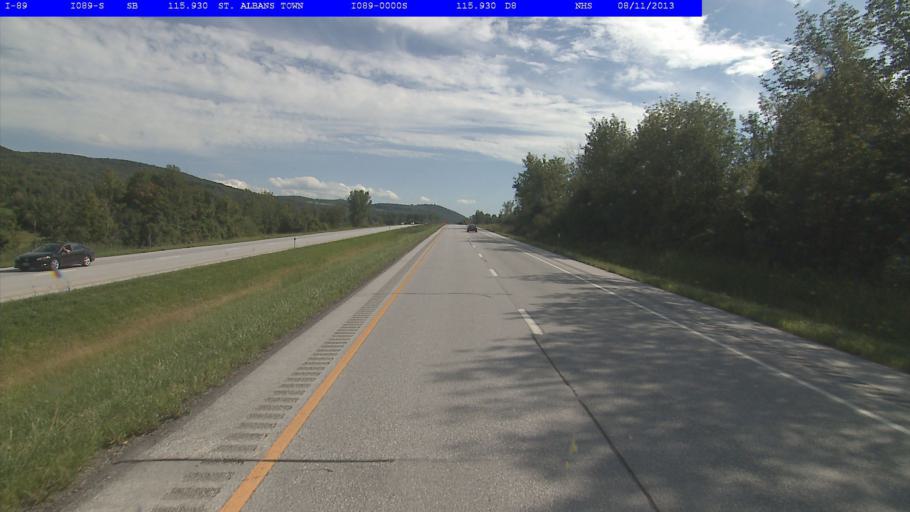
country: US
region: Vermont
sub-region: Franklin County
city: Saint Albans
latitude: 44.8258
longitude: -73.0624
